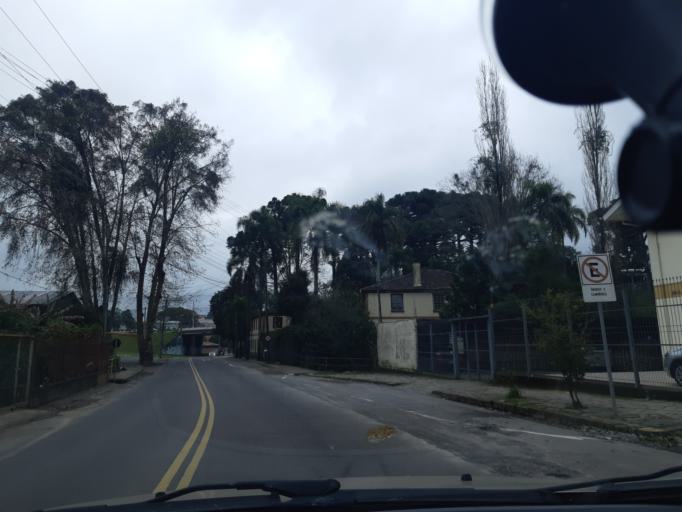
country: BR
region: Rio Grande do Sul
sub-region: Caxias Do Sul
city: Caxias do Sul
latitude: -29.1573
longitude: -51.2005
